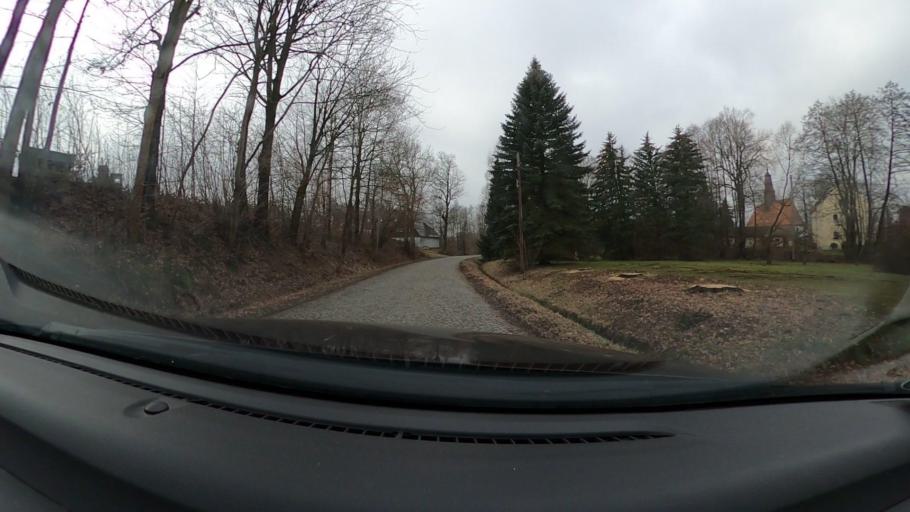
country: DE
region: Saxony
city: Oberschona
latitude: 50.9062
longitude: 13.2882
